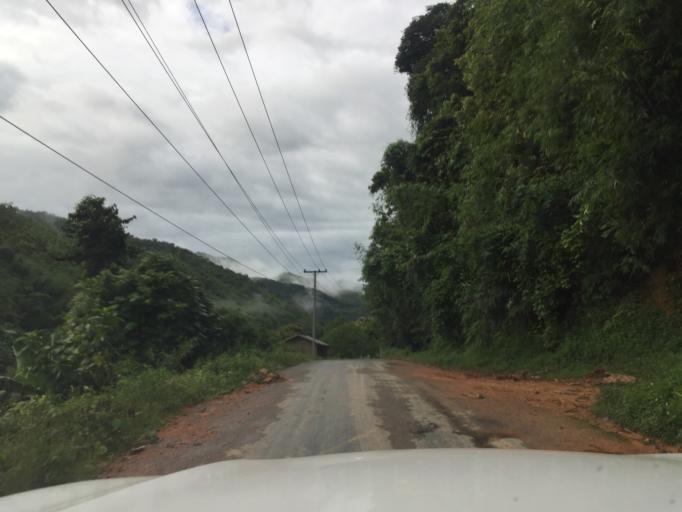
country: LA
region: Oudomxai
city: Muang La
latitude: 21.0858
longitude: 102.2422
